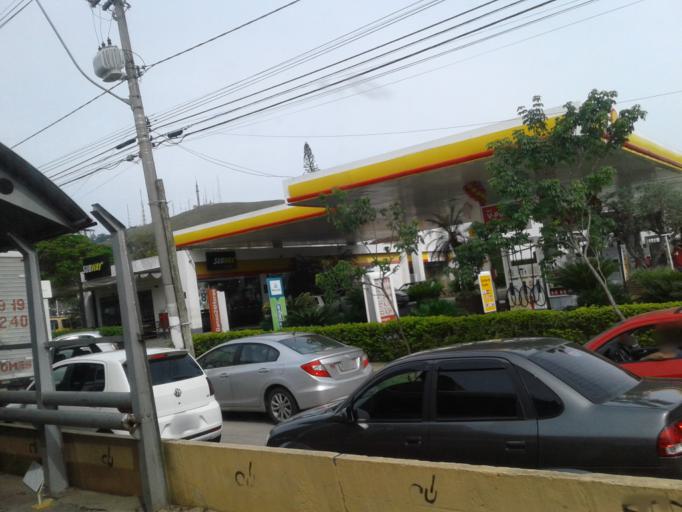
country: BR
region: Rio Grande do Sul
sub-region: Porto Alegre
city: Porto Alegre
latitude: -30.0736
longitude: -51.2003
